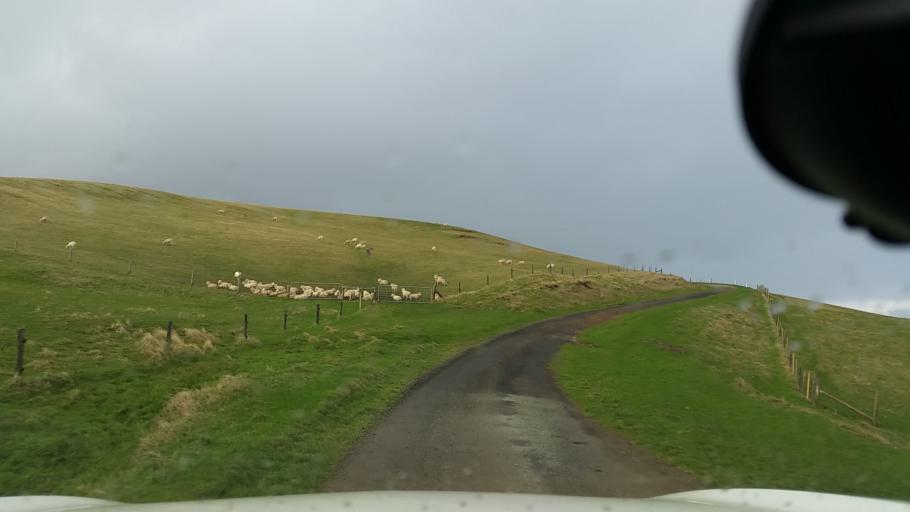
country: NZ
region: Chatham Islands
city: Waitangi
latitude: -44.0380
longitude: -176.6460
